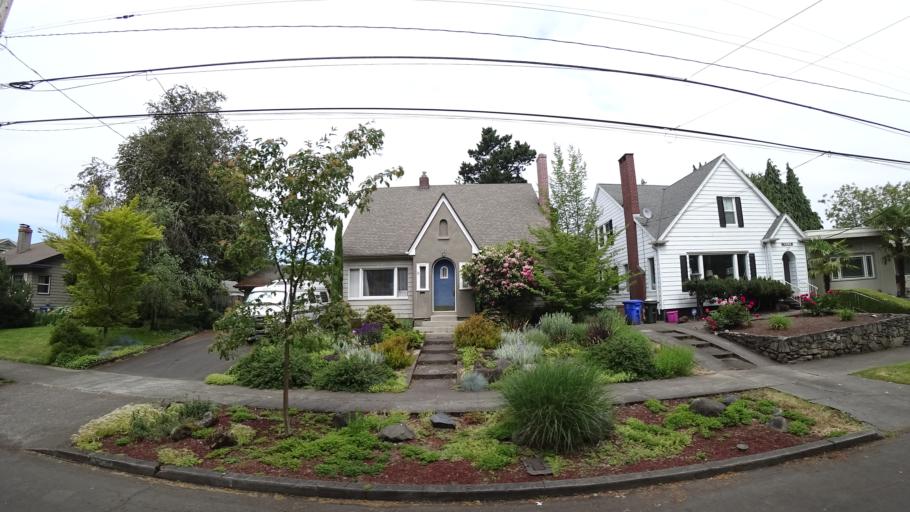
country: US
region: Oregon
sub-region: Multnomah County
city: Portland
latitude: 45.5307
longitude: -122.6179
